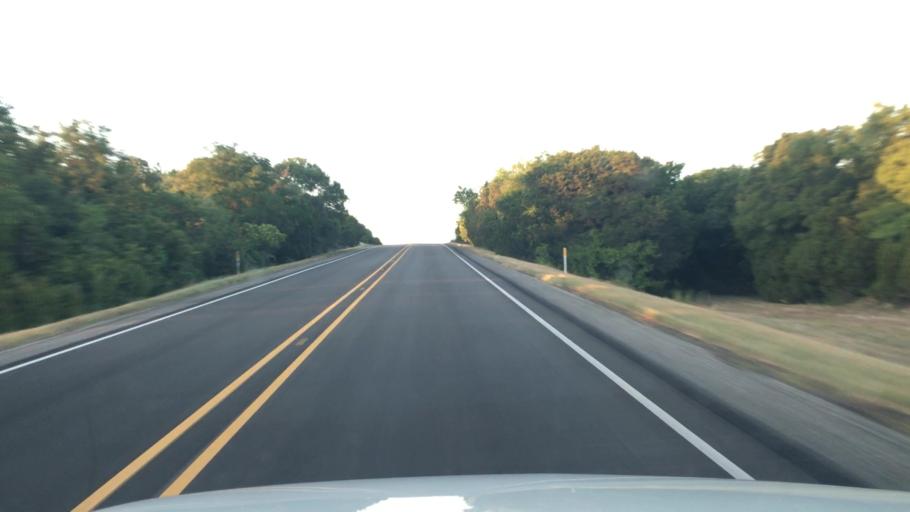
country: US
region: Texas
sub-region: Hamilton County
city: Hico
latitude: 32.0986
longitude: -97.9649
